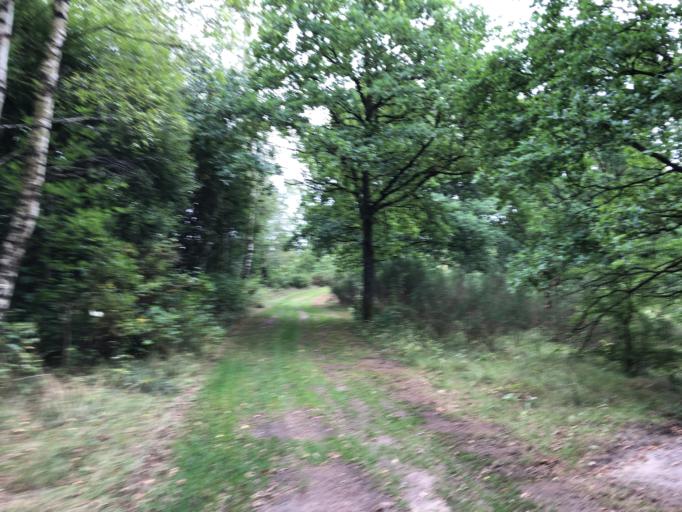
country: DK
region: Central Jutland
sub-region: Herning Kommune
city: Lind
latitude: 56.0595
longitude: 8.9883
